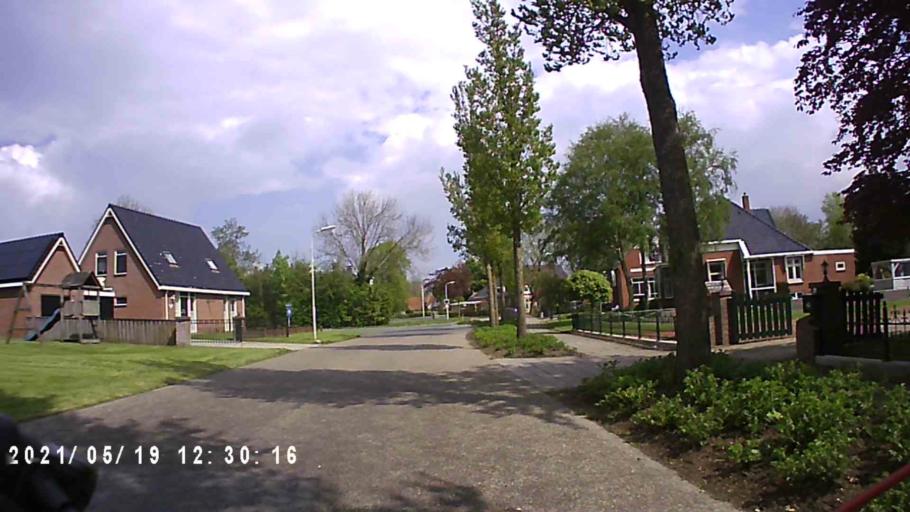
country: NL
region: Groningen
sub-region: Gemeente Grootegast
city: Grootegast
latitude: 53.2720
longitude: 6.2289
